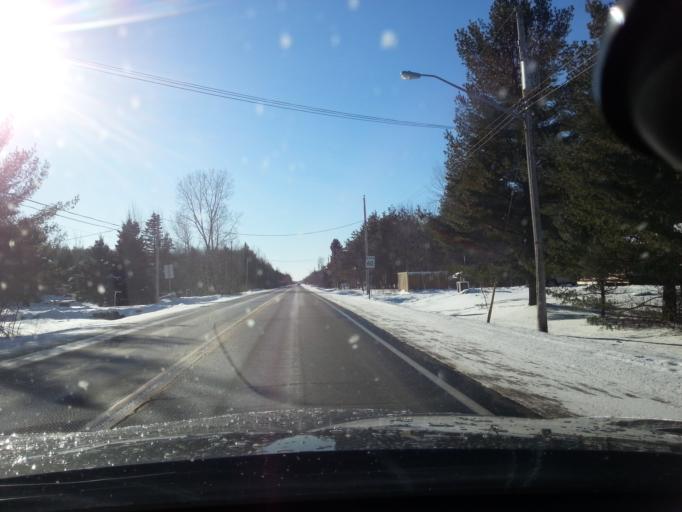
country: CA
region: Ontario
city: Ottawa
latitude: 45.3210
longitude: -75.4711
